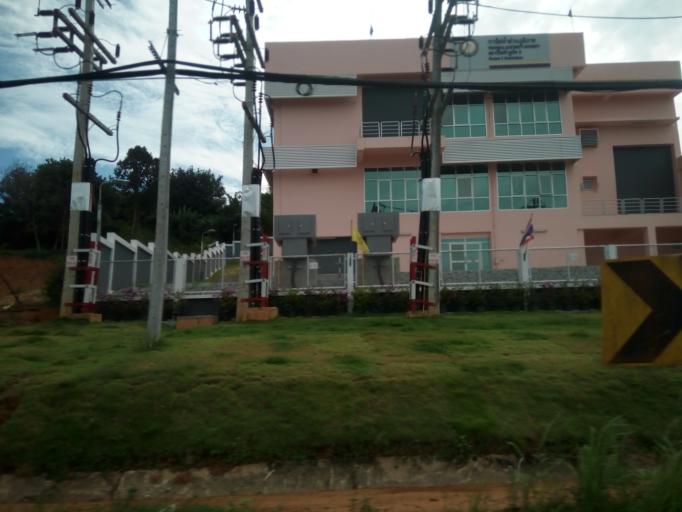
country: TH
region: Phuket
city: Mueang Phuket
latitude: 7.8425
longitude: 98.3863
